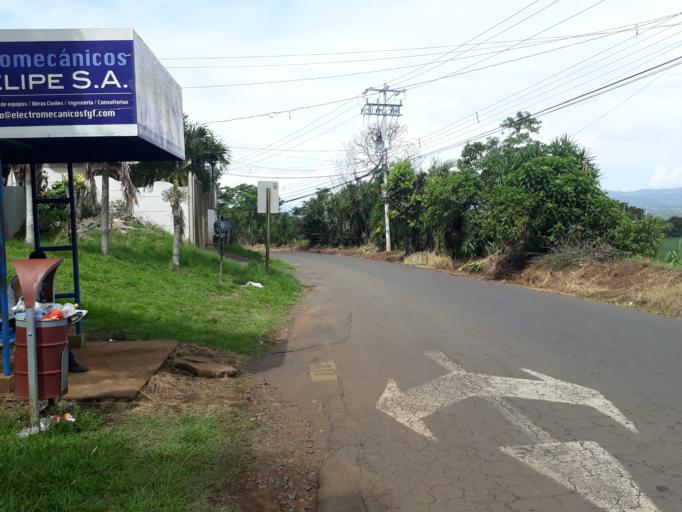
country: CR
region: Alajuela
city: Carrillos
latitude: 10.0280
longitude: -84.3298
